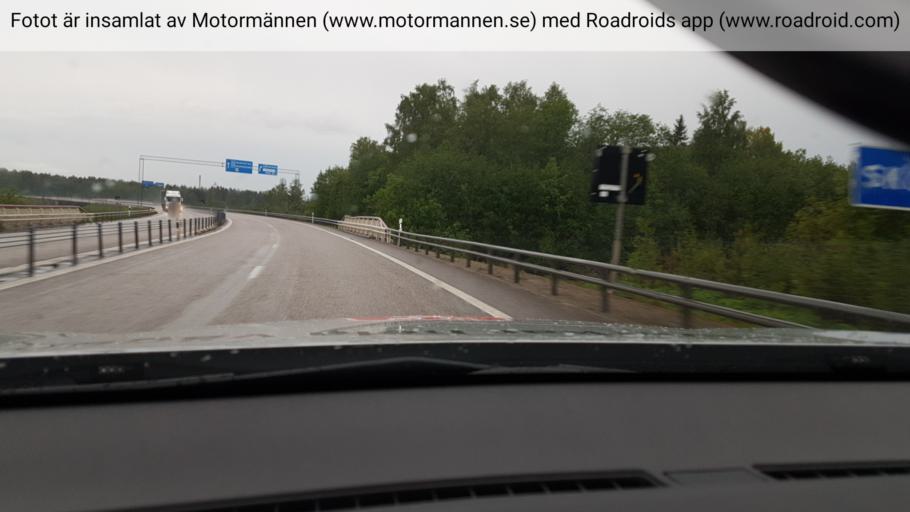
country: SE
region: Vaestra Goetaland
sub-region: Skovde Kommun
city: Skultorp
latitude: 58.3587
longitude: 13.8654
